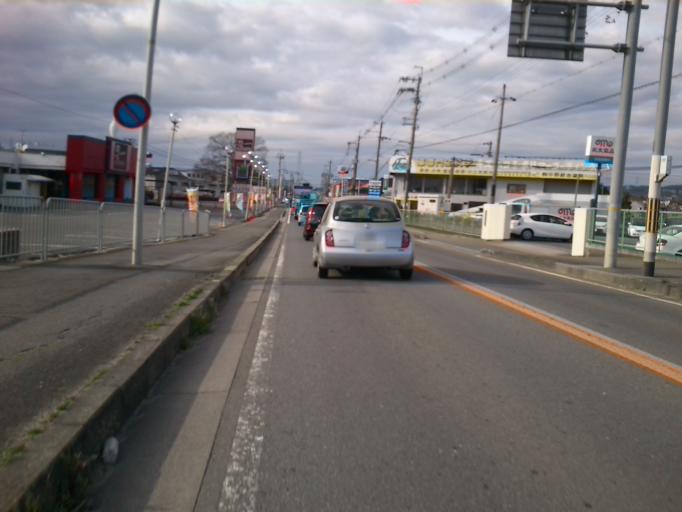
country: JP
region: Kyoto
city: Tanabe
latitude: 34.8250
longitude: 135.7941
